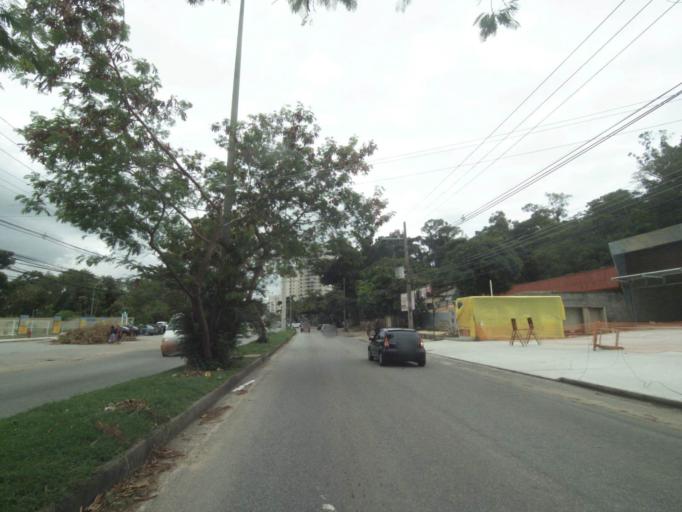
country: BR
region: Rio de Janeiro
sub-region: Nilopolis
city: Nilopolis
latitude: -22.9654
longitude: -43.4086
